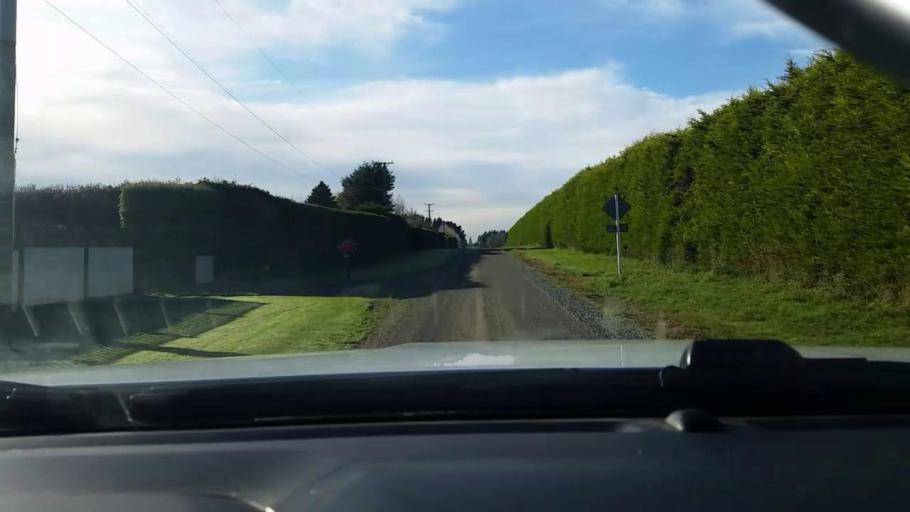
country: NZ
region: Southland
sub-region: Invercargill City
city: Invercargill
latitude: -46.2845
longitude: 168.3434
